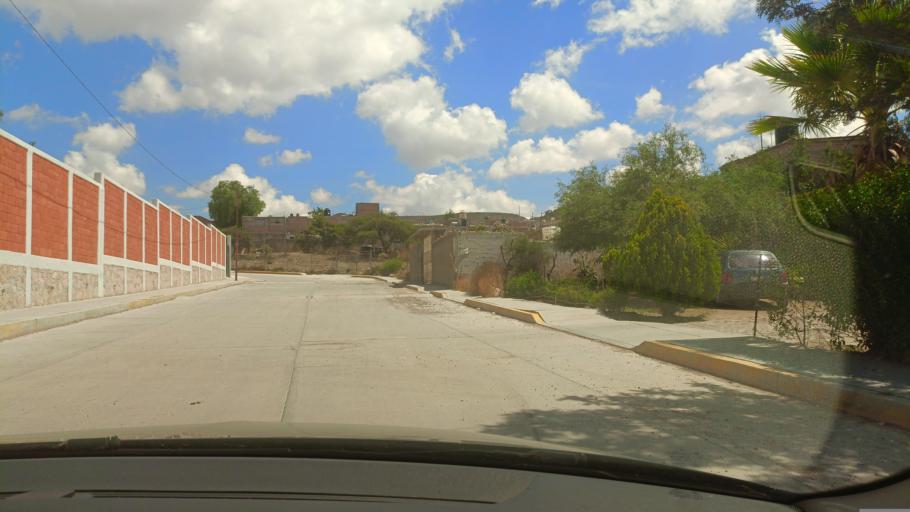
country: MX
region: Guanajuato
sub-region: San Luis de la Paz
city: San Luis de la Paz
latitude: 21.3028
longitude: -100.5049
